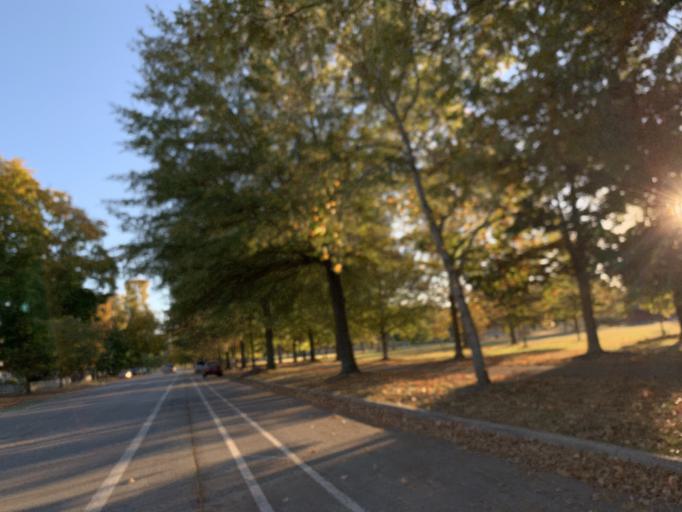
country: US
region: Indiana
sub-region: Floyd County
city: New Albany
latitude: 38.2633
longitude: -85.8265
